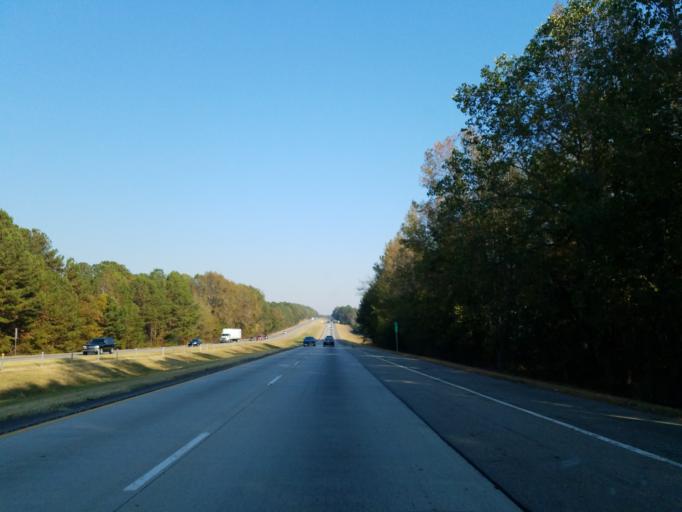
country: US
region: Georgia
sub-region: Bibb County
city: West Point
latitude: 32.9398
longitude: -83.7744
